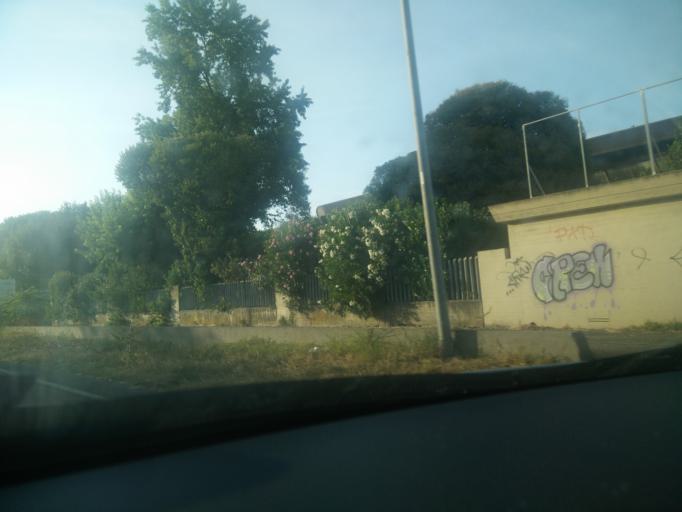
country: IT
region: Tuscany
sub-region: Provincia di Massa-Carrara
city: Massa
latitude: 44.0310
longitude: 10.0992
